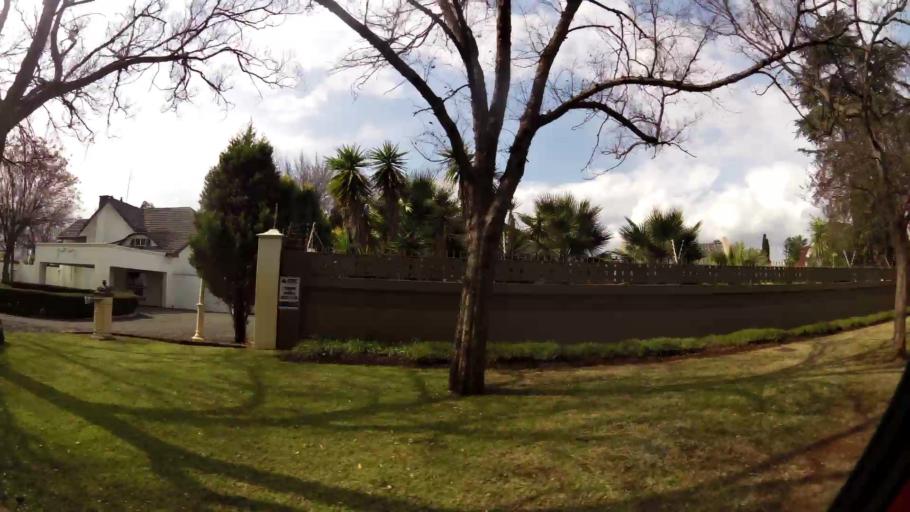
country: ZA
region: Gauteng
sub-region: Sedibeng District Municipality
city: Vanderbijlpark
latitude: -26.7371
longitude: 27.8360
